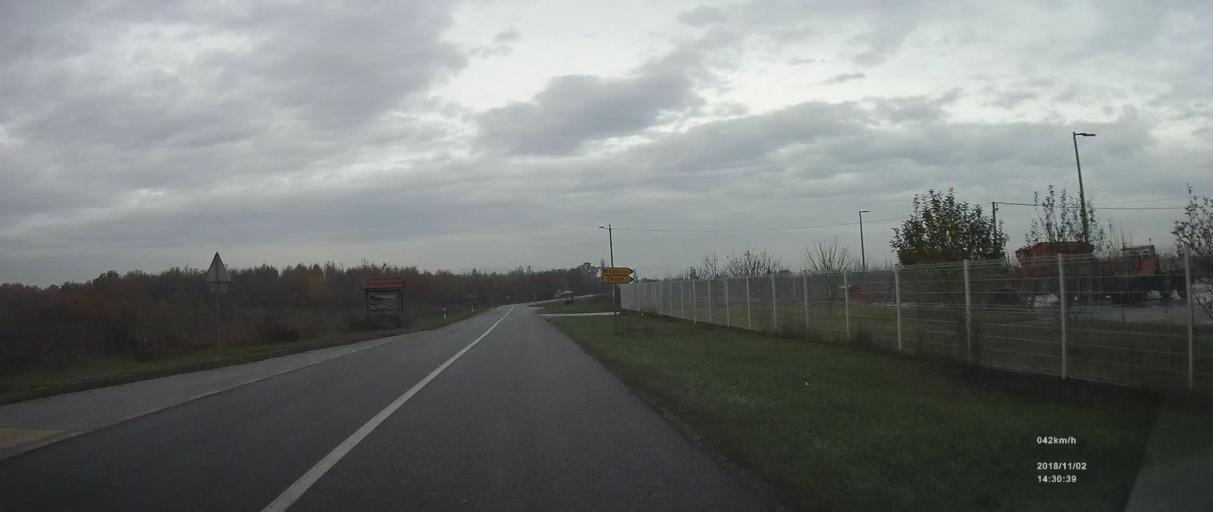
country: HR
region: Zagrebacka
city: Gradici
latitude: 45.6799
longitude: 16.0567
